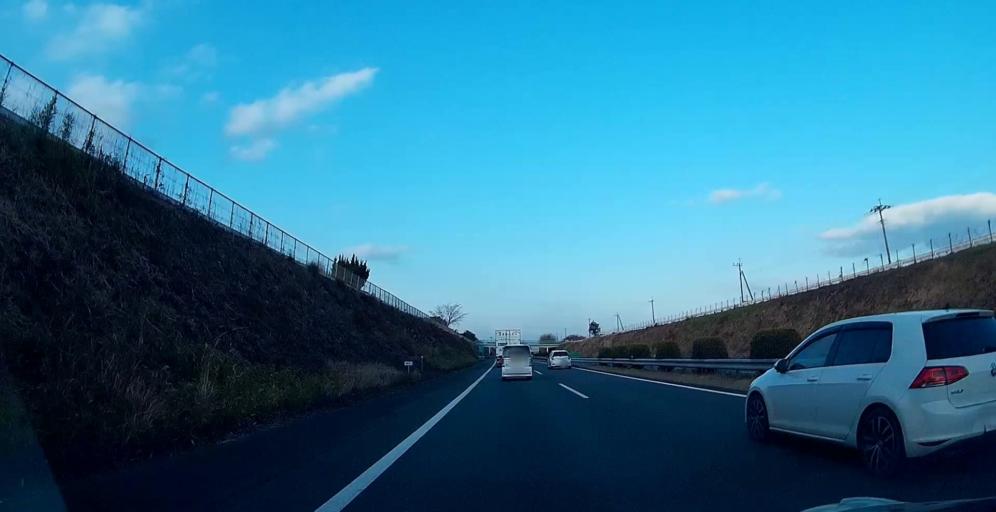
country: JP
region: Kumamoto
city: Uto
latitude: 32.7028
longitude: 130.7523
